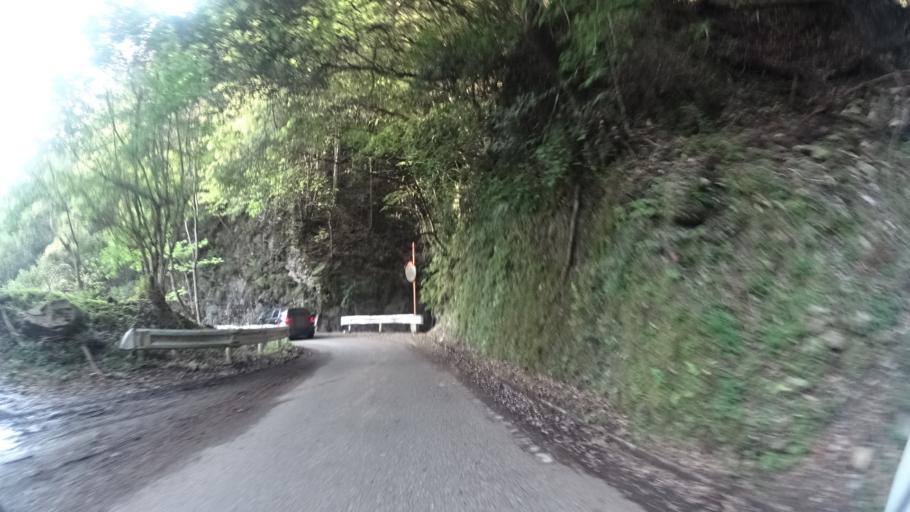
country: JP
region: Tokushima
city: Ikedacho
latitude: 33.9449
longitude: 133.8079
